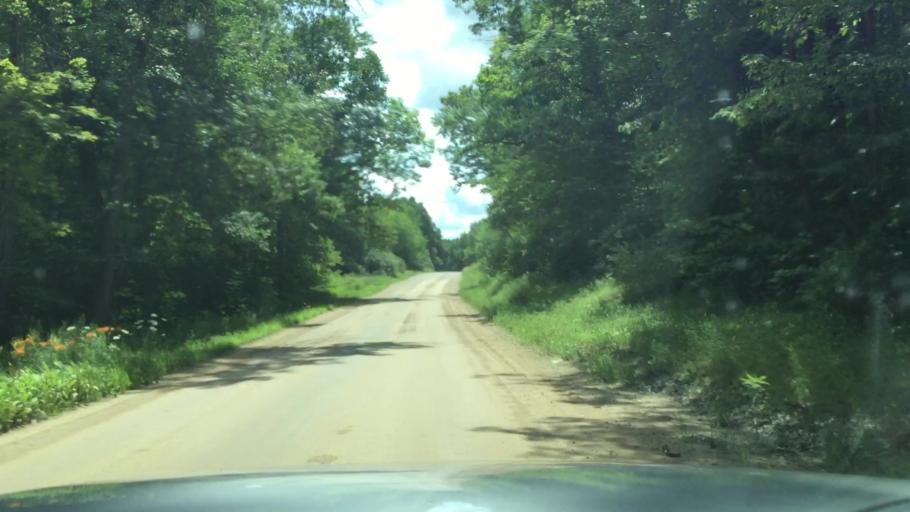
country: US
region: Michigan
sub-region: Ionia County
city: Belding
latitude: 43.1174
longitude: -85.2108
